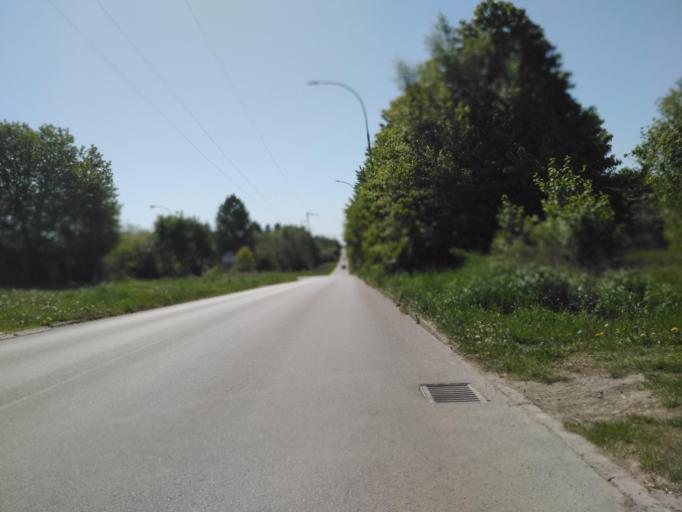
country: PL
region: Subcarpathian Voivodeship
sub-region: Krosno
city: Krosno
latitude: 49.6785
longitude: 21.7825
